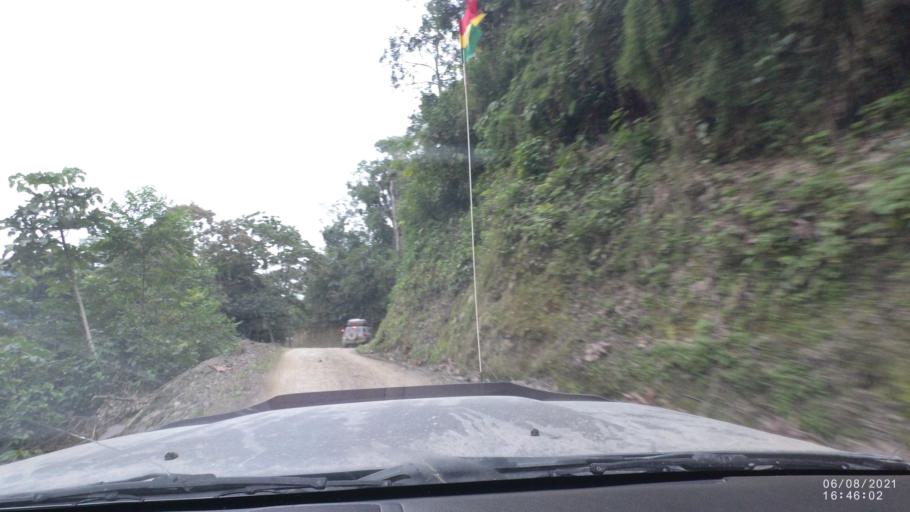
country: BO
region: La Paz
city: Quime
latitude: -16.5062
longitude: -66.7588
